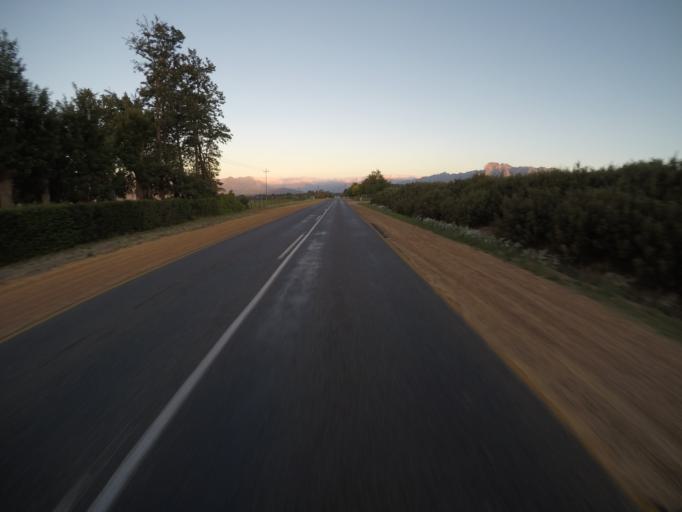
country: ZA
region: Western Cape
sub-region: Cape Winelands District Municipality
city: Paarl
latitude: -33.8287
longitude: 18.9413
